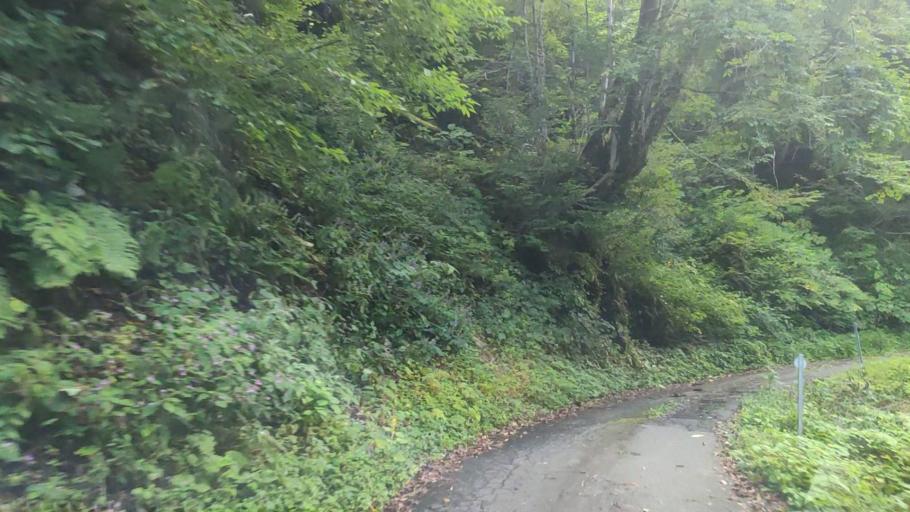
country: JP
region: Gifu
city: Takayama
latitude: 36.3125
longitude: 137.0878
